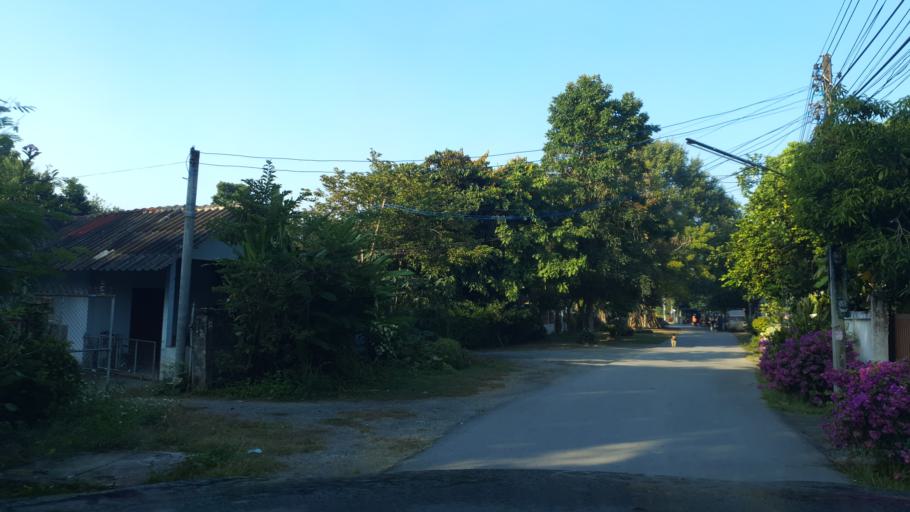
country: TH
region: Chiang Mai
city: San Kamphaeng
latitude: 18.7206
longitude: 99.1501
